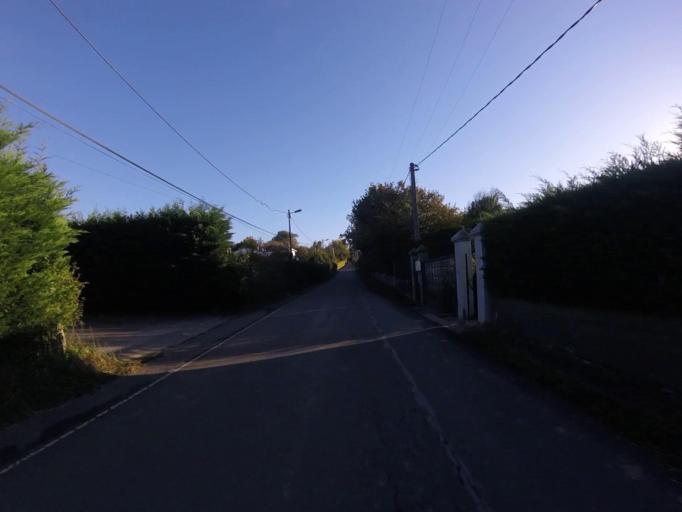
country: ES
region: Basque Country
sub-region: Provincia de Guipuzcoa
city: Lasarte
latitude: 43.2900
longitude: -2.0152
